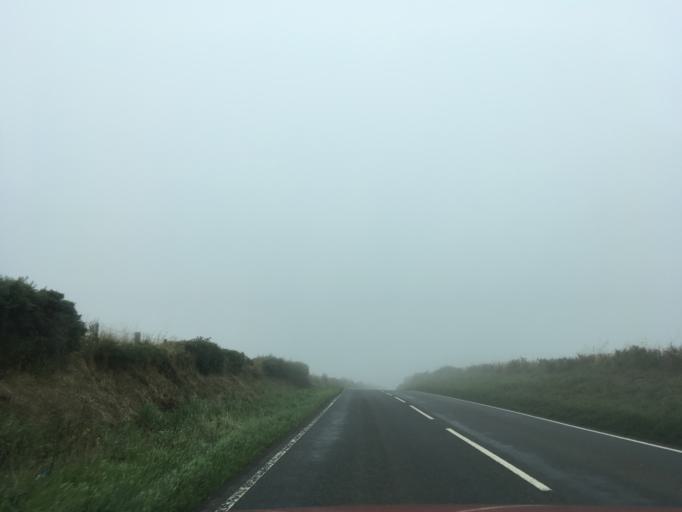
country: GB
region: Wales
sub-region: Pembrokeshire
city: Llanrhian
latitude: 51.8686
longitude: -5.1357
